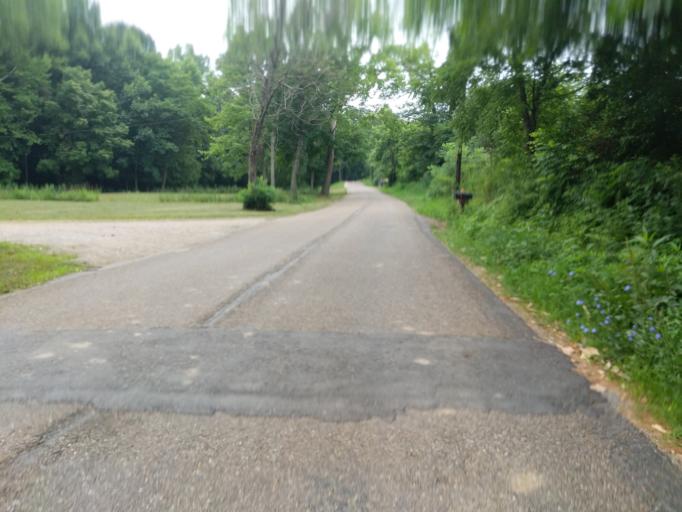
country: US
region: Ohio
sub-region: Athens County
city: The Plains
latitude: 39.3821
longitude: -82.1442
